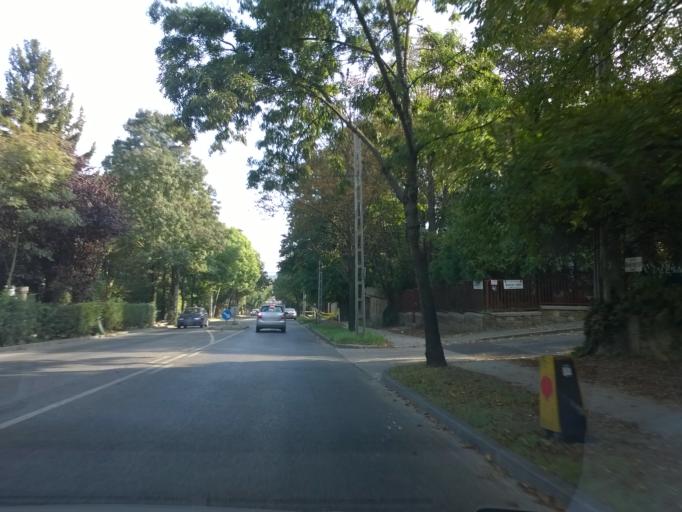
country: HU
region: Budapest
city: Budapest XII. keruelet
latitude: 47.5252
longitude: 18.9853
